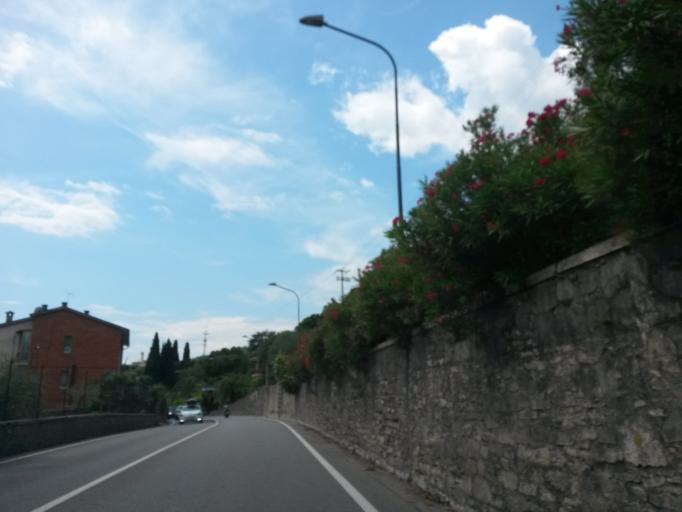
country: IT
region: Lombardy
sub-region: Provincia di Brescia
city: Gargnano
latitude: 45.6822
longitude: 10.6552
